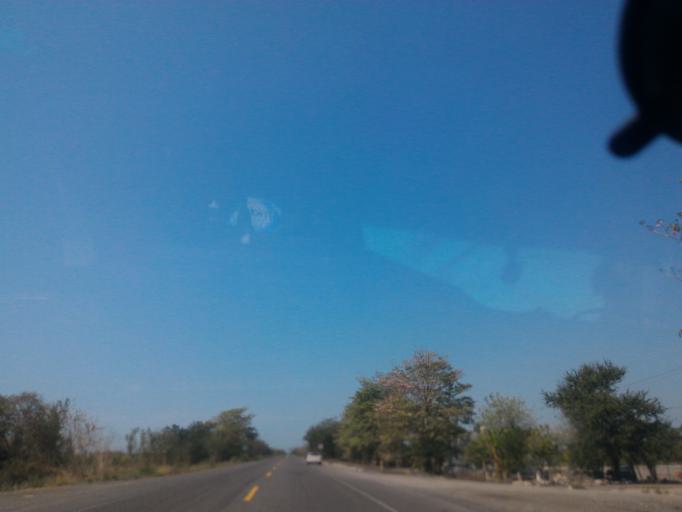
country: MX
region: Michoacan
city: Coahuayana Viejo
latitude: 18.7779
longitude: -103.7568
